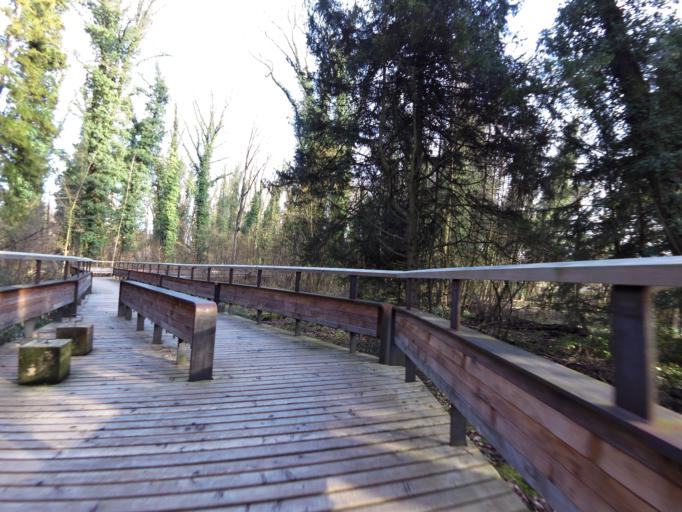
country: CH
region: Zurich
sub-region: Bezirk Zuerich
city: Zuerich (Kreis 10) / Ruetihof
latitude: 47.4030
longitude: 8.4794
